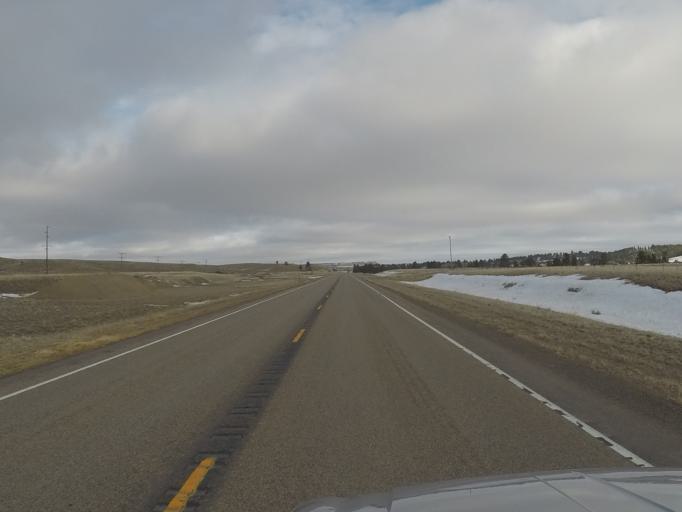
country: US
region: Montana
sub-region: Golden Valley County
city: Ryegate
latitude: 46.3045
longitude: -109.3428
